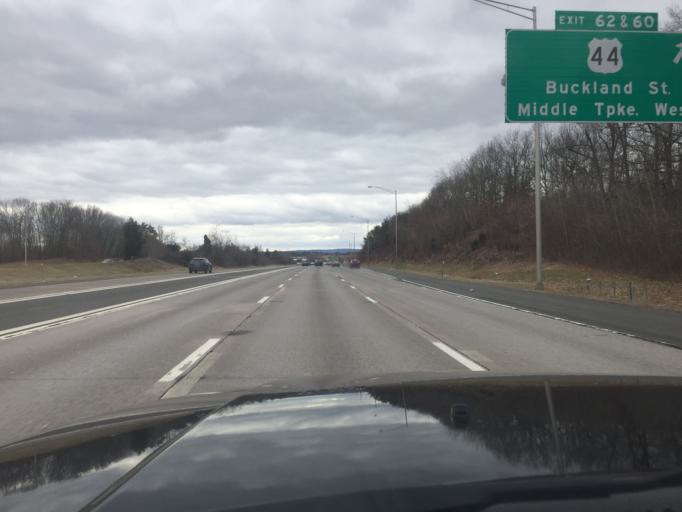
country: US
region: Connecticut
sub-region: Hartford County
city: Manchester
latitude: 41.8041
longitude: -72.5430
